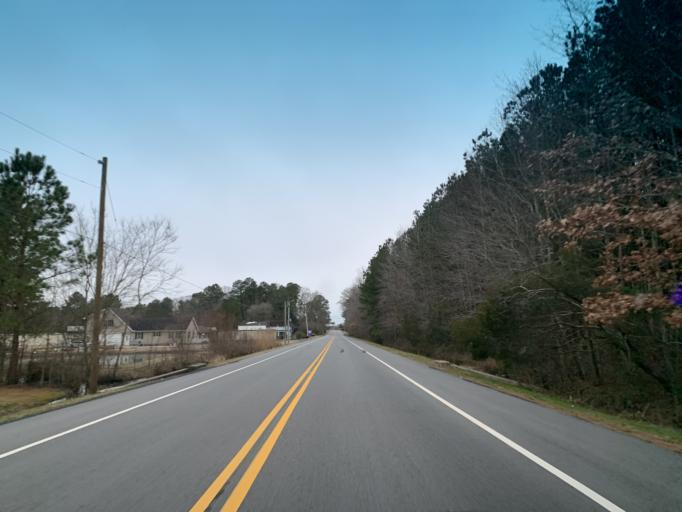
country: US
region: Maryland
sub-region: Worcester County
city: Pocomoke City
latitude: 38.0740
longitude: -75.5459
